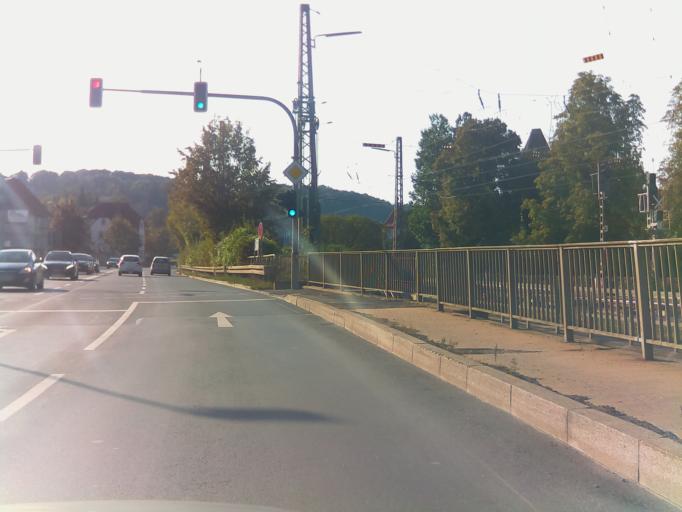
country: DE
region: Bavaria
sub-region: Regierungsbezirk Unterfranken
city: Ochsenfurt
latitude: 49.6627
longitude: 10.0689
